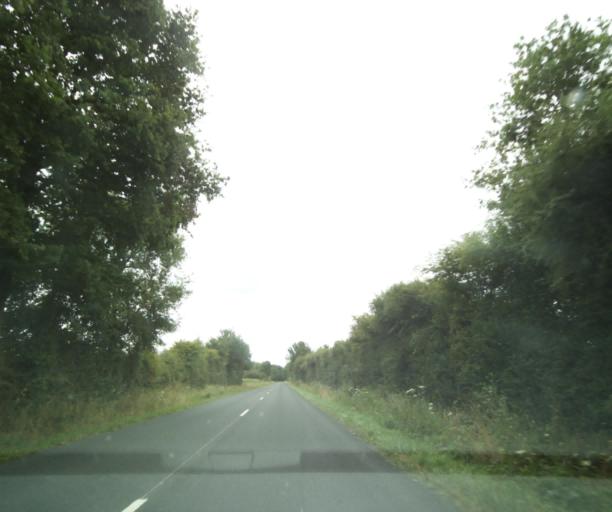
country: FR
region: Pays de la Loire
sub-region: Departement de la Sarthe
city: Precigne
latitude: 47.7491
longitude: -0.2945
